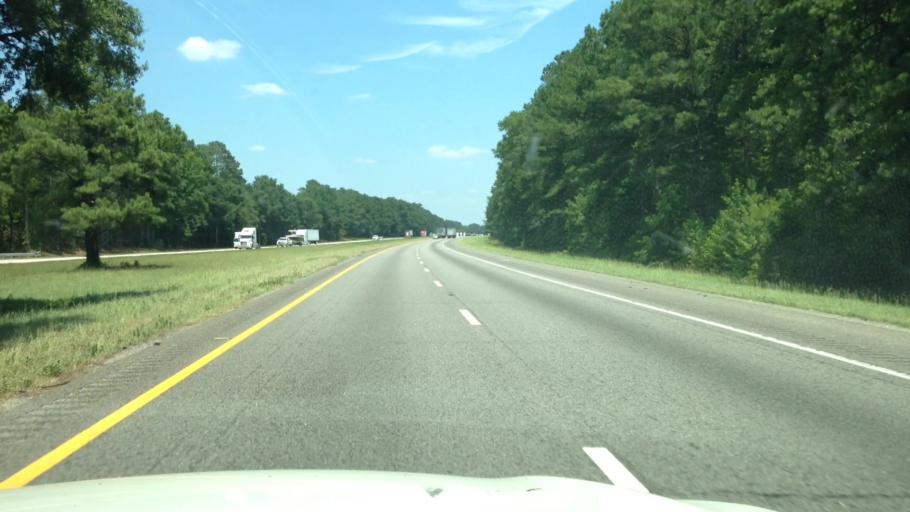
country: US
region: South Carolina
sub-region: Dillon County
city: Latta
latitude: 34.4034
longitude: -79.4432
